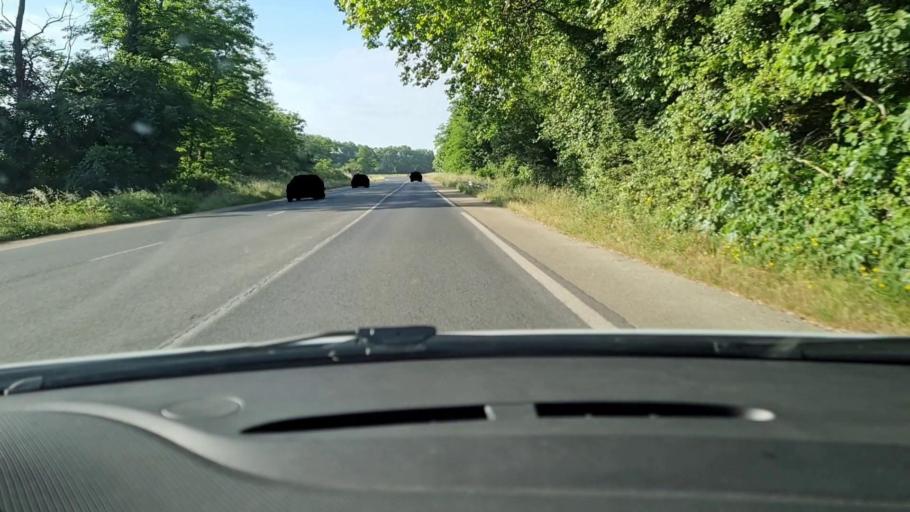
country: FR
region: Languedoc-Roussillon
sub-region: Departement du Gard
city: Bellegarde
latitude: 43.7670
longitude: 4.4747
